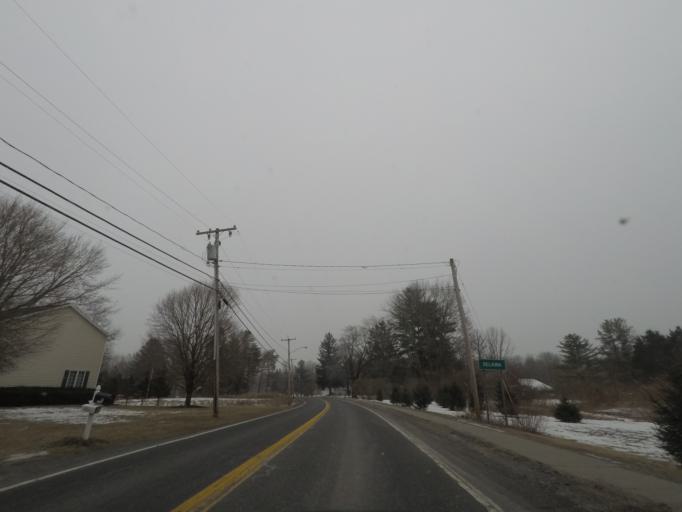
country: US
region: New York
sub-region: Rensselaer County
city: Castleton-on-Hudson
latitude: 42.5396
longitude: -73.8019
